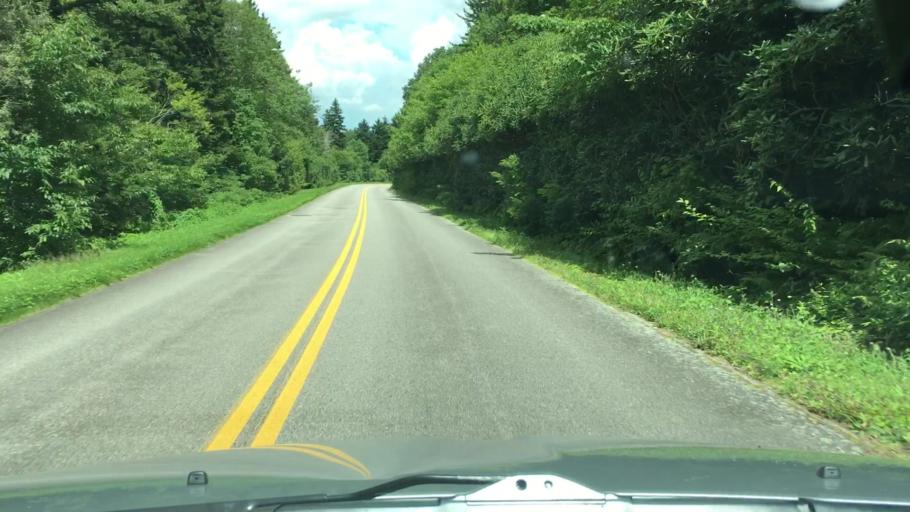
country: US
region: North Carolina
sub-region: Buncombe County
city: Black Mountain
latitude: 35.7072
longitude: -82.2703
